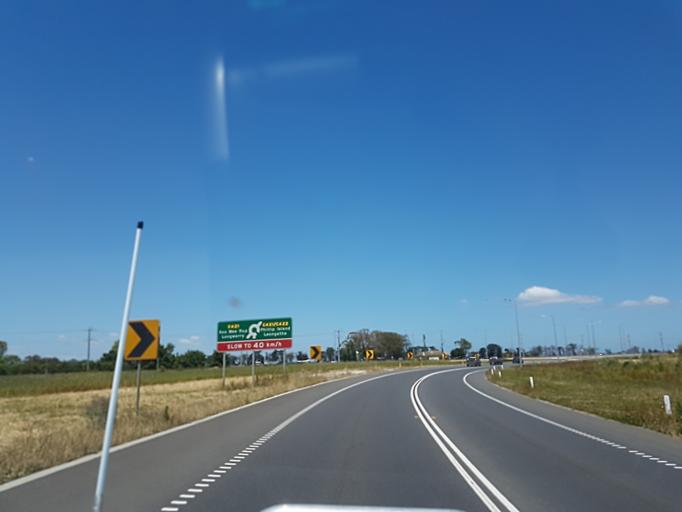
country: AU
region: Victoria
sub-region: Cardinia
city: Koo-Wee-Rup
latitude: -38.2061
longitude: 145.4738
